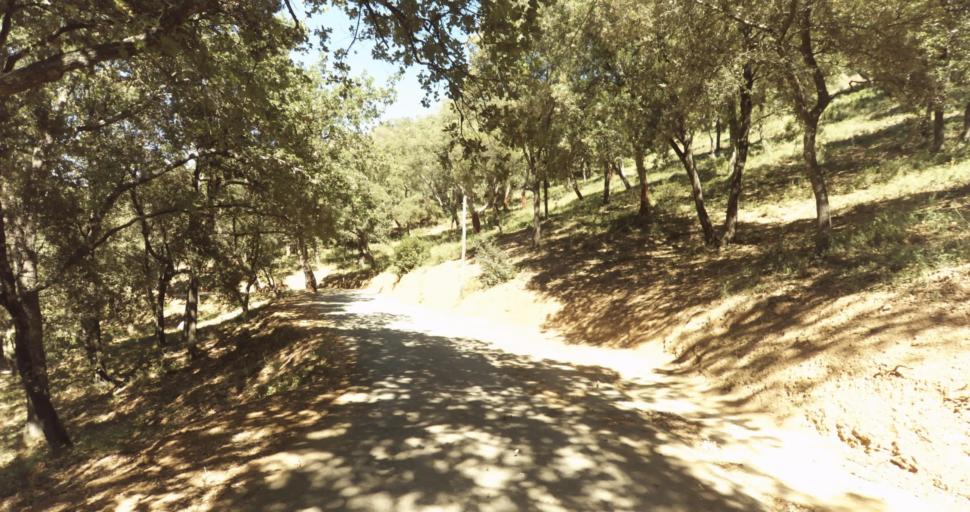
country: FR
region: Provence-Alpes-Cote d'Azur
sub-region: Departement du Var
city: La Croix-Valmer
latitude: 43.2263
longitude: 6.5599
